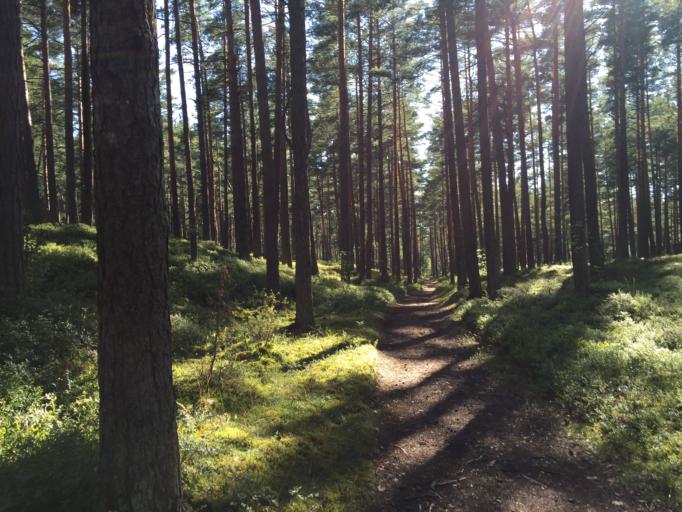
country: LV
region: Riga
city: Jaunciems
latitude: 57.0825
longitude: 24.1406
